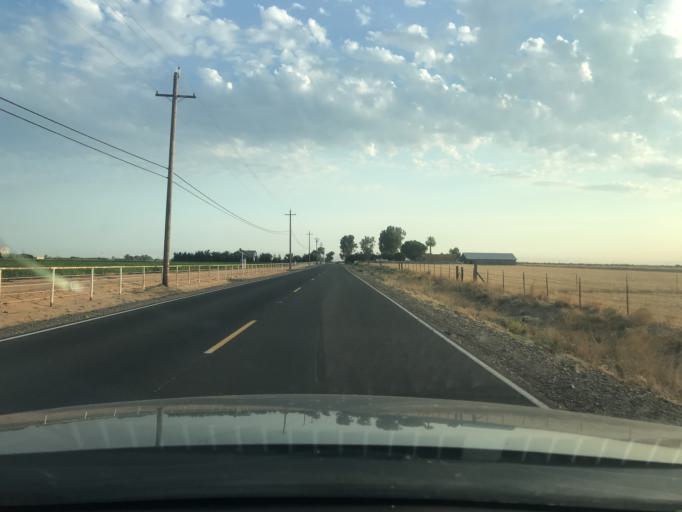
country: US
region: California
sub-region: Merced County
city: Atwater
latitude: 37.3542
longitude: -120.5404
